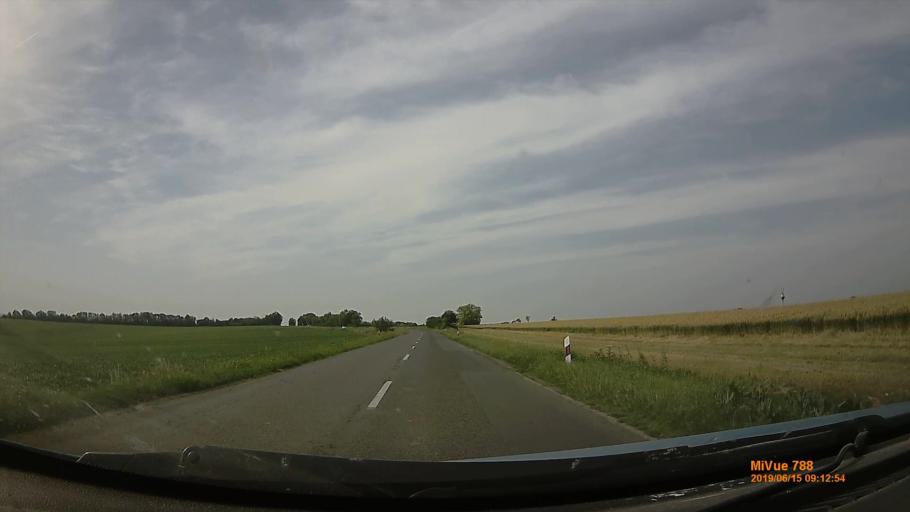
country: HU
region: Tolna
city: Iregszemcse
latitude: 46.6606
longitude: 18.1874
